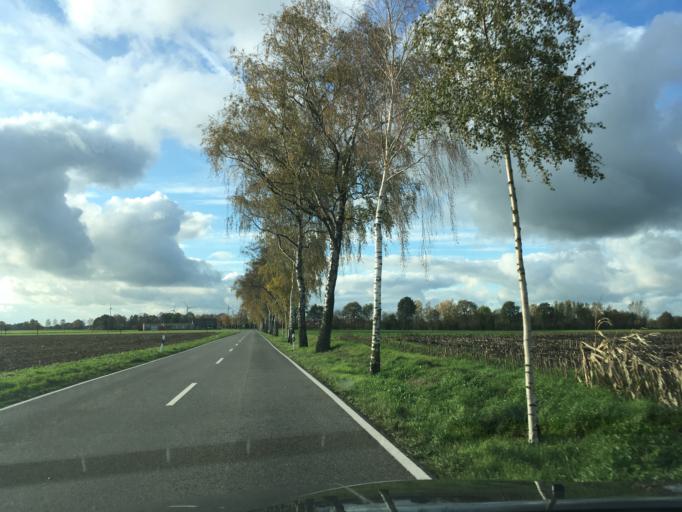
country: DE
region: North Rhine-Westphalia
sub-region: Regierungsbezirk Munster
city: Vreden
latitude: 52.0995
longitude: 6.8747
